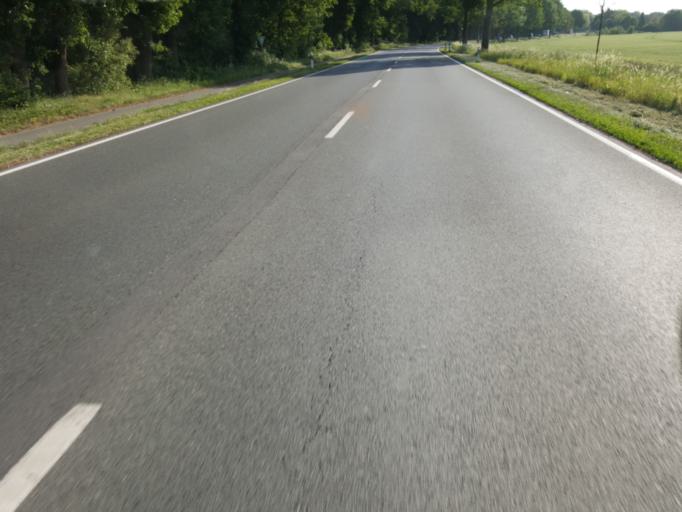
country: DE
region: Lower Saxony
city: Estorf
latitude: 52.6040
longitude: 9.1654
